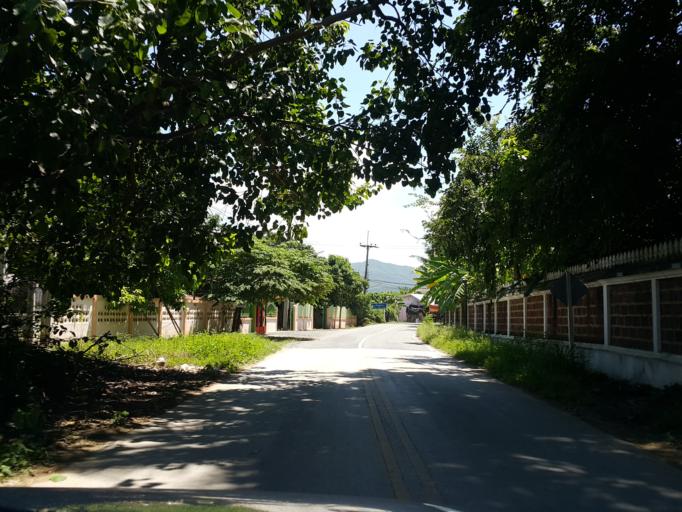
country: TH
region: Lamphun
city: Ban Thi
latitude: 18.6686
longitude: 99.1512
